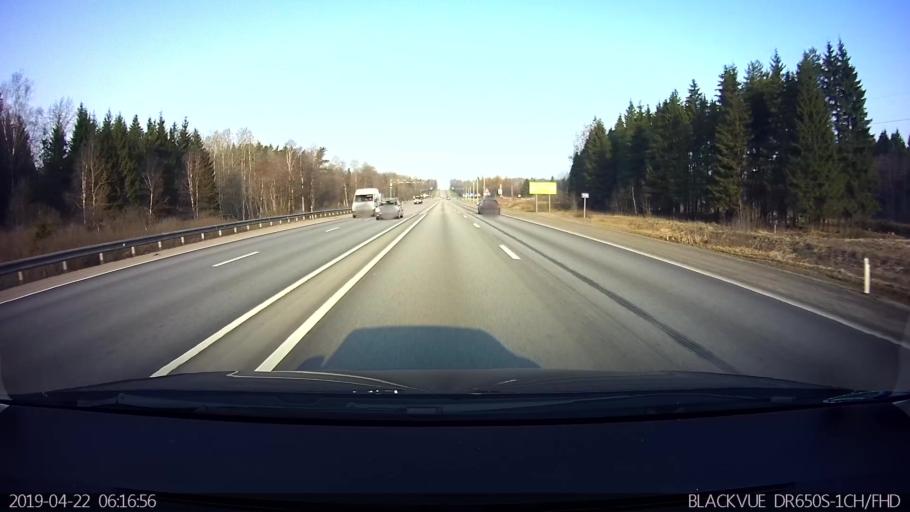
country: RU
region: Moskovskaya
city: Mozhaysk
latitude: 55.4609
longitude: 36.0049
